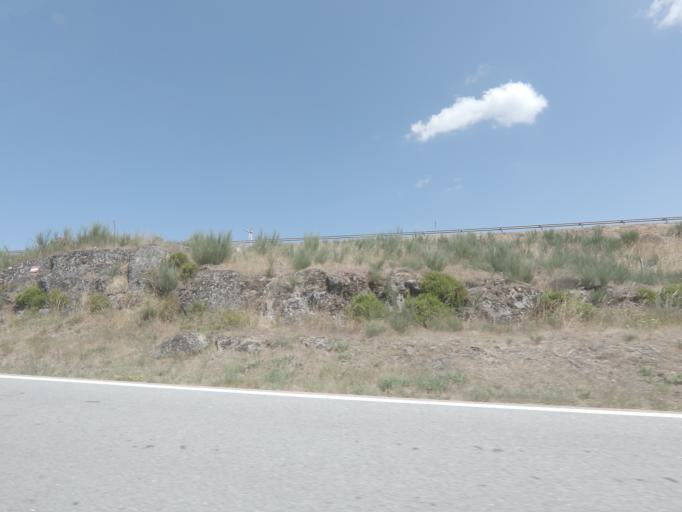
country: PT
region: Viseu
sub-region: Tarouca
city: Tarouca
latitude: 40.9931
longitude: -7.8825
